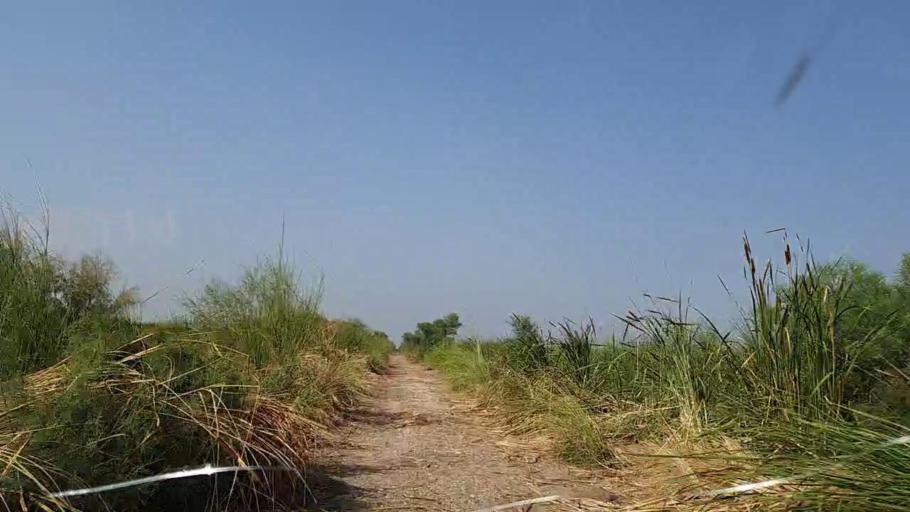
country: PK
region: Sindh
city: Khanpur
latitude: 27.6802
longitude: 69.3778
